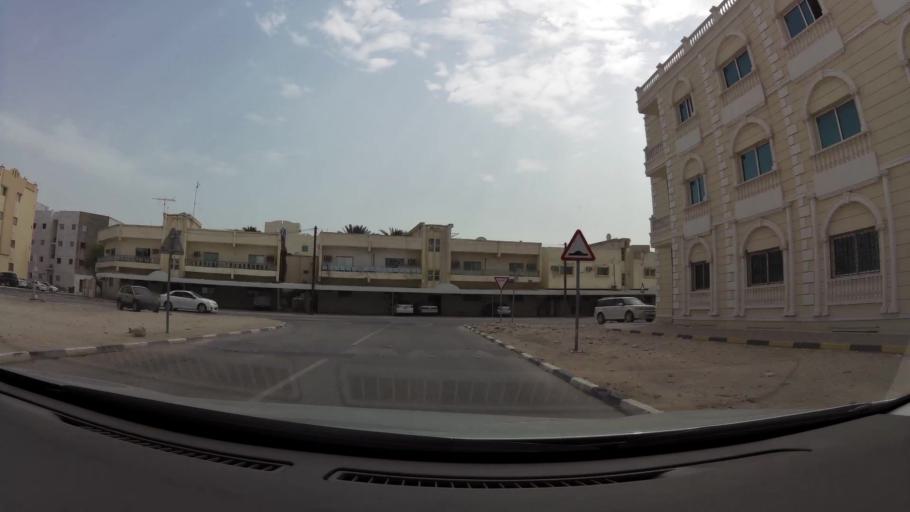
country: QA
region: Baladiyat ad Dawhah
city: Doha
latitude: 25.3038
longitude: 51.4930
